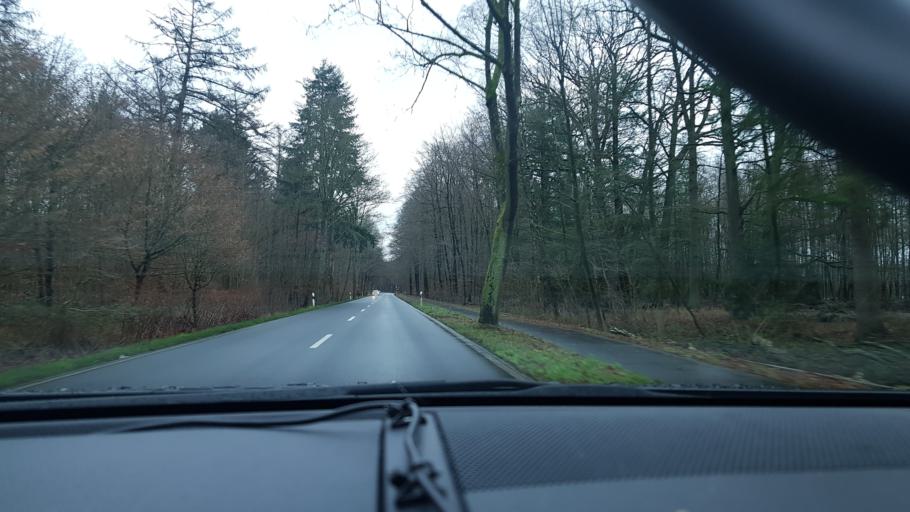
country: NL
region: Limburg
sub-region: Gemeente Beesel
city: Offenbeek
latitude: 51.2328
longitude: 6.1106
